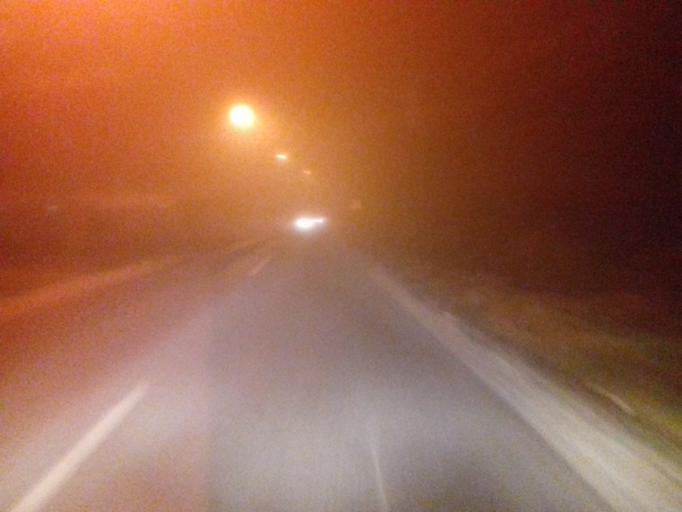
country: BA
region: Federation of Bosnia and Herzegovina
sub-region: Kanton Sarajevo
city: Sarajevo
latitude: 43.7852
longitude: 18.3607
